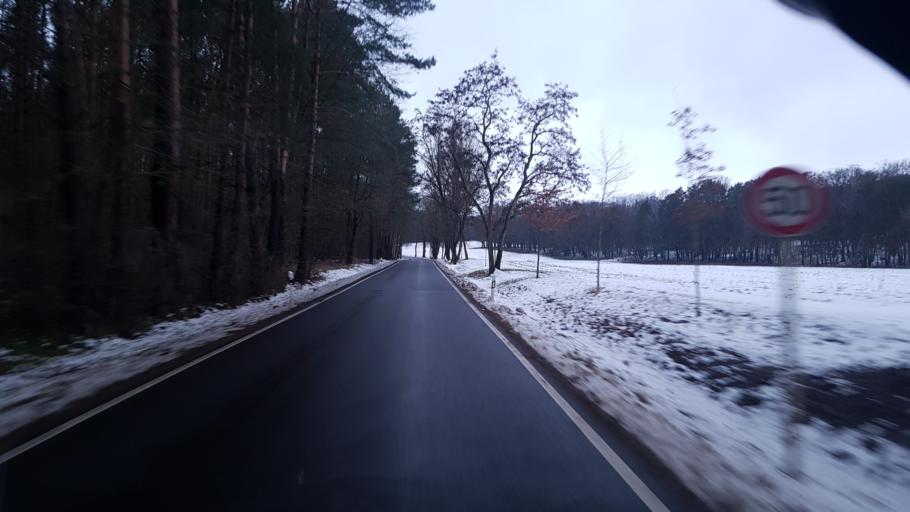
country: DE
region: Brandenburg
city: Gross Lindow
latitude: 52.2800
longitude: 14.5253
